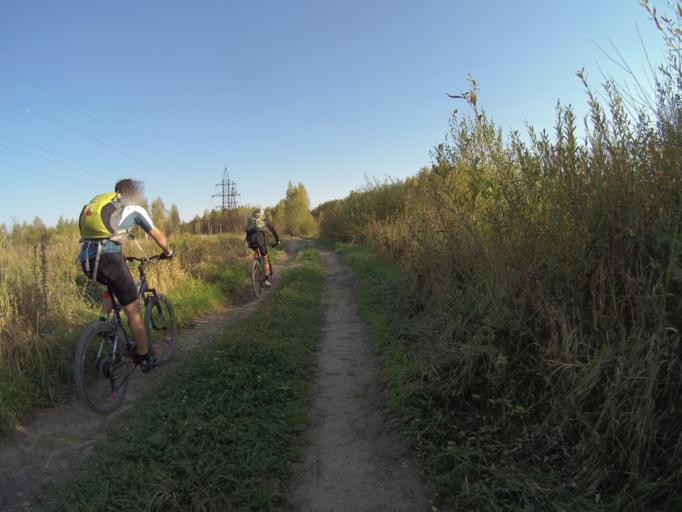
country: RU
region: Vladimir
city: Raduzhnyy
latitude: 56.0151
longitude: 40.3932
